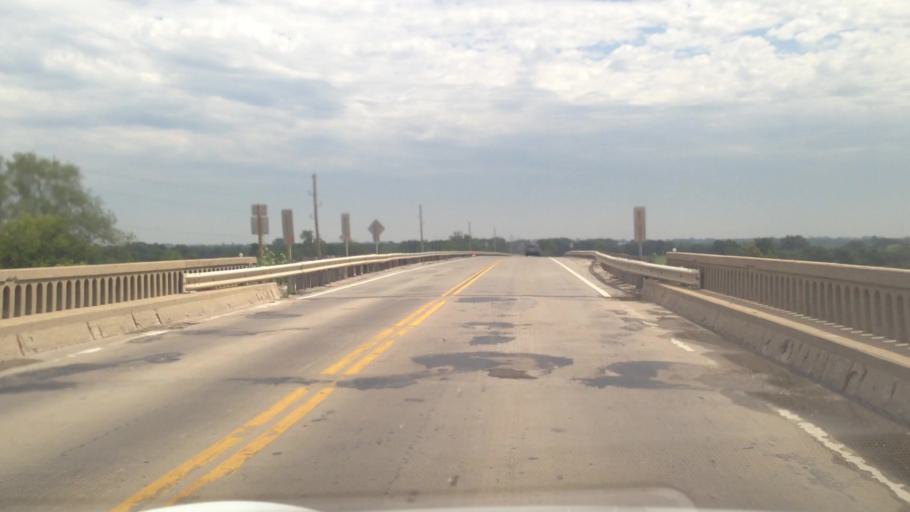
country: US
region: Kansas
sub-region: Allen County
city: Iola
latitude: 37.9216
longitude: -95.1656
